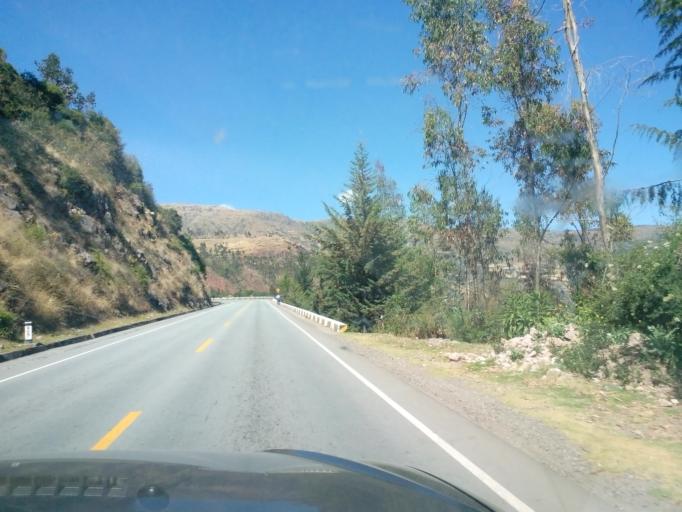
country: PE
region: Cusco
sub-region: Provincia de Anta
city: Limatambo
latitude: -13.4468
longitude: -72.4007
